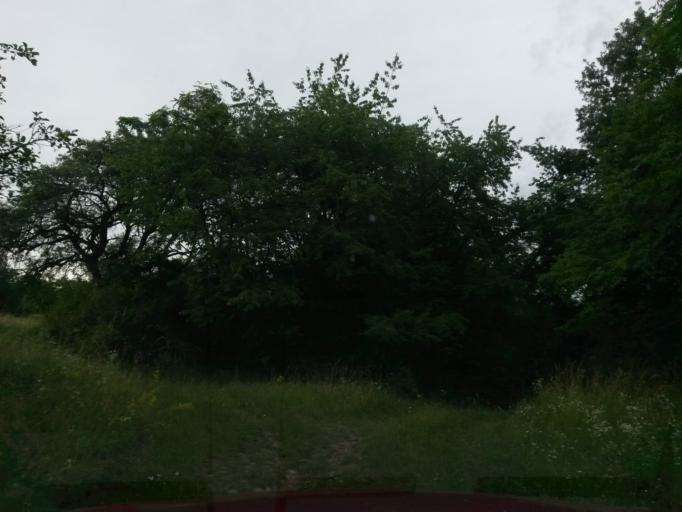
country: SK
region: Banskobystricky
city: Velky Krtis
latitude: 48.3275
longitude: 19.4244
